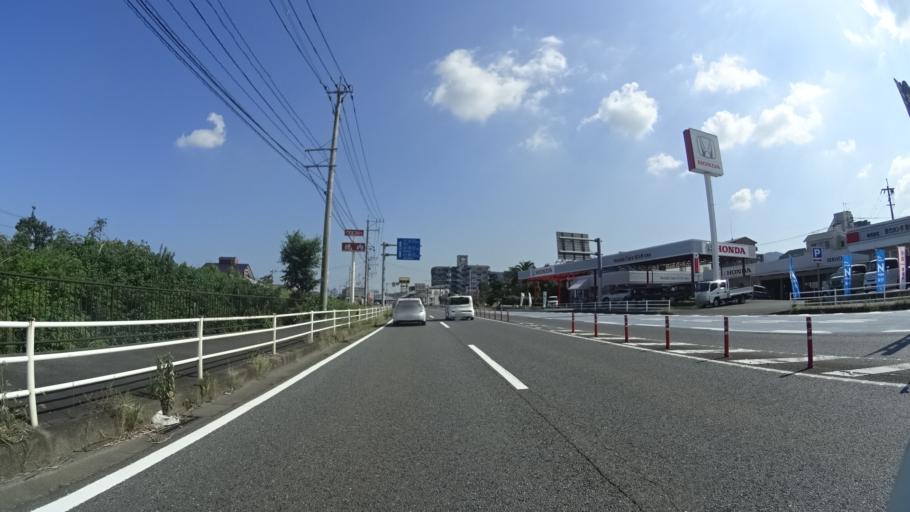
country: JP
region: Fukuoka
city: Kanda
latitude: 33.8096
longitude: 130.9555
